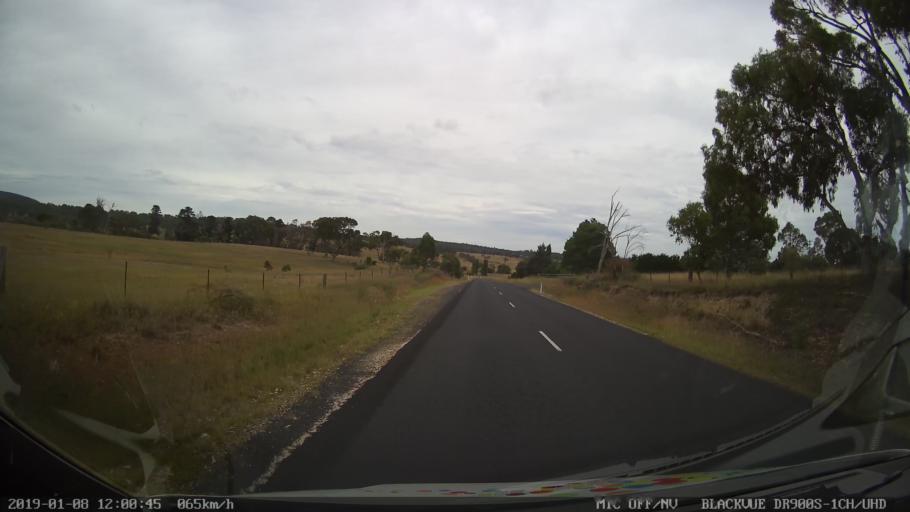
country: AU
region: New South Wales
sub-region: Armidale Dumaresq
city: Armidale
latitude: -30.4609
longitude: 151.6050
